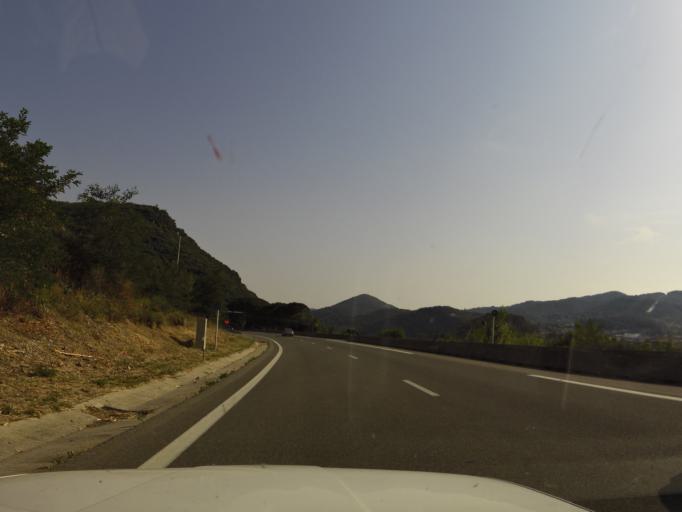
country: FR
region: Languedoc-Roussillon
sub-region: Departement de l'Herault
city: Lodeve
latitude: 43.7329
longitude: 3.3268
